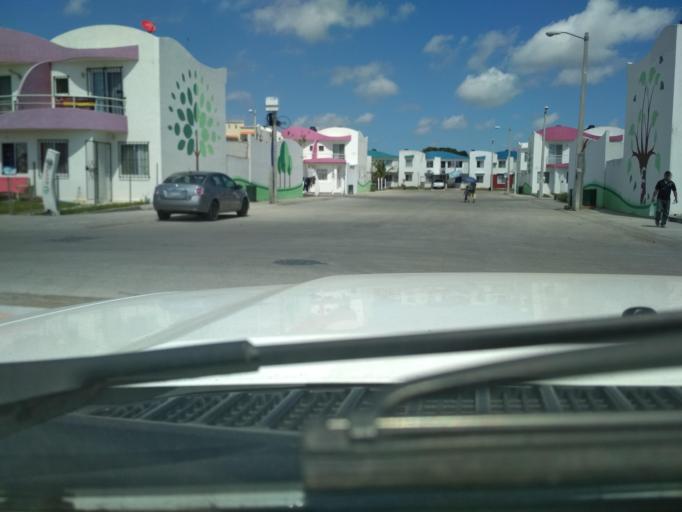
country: MX
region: Veracruz
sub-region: Veracruz
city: Las Amapolas
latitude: 19.1332
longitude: -96.2055
